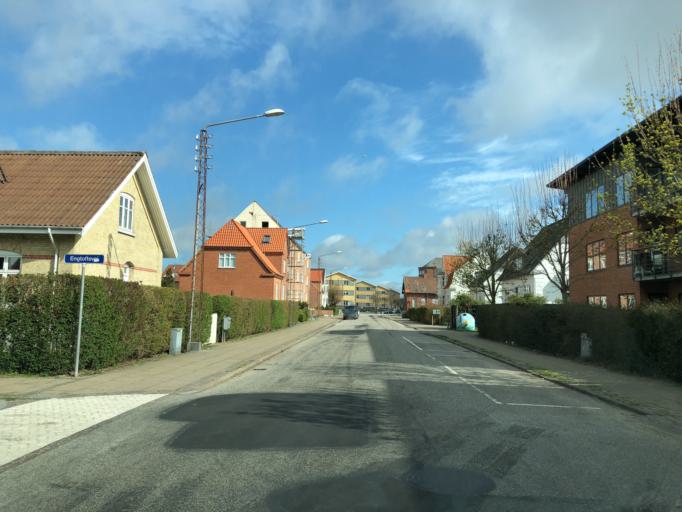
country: DK
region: North Denmark
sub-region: Alborg Kommune
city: Aalborg
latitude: 57.0535
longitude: 9.8966
